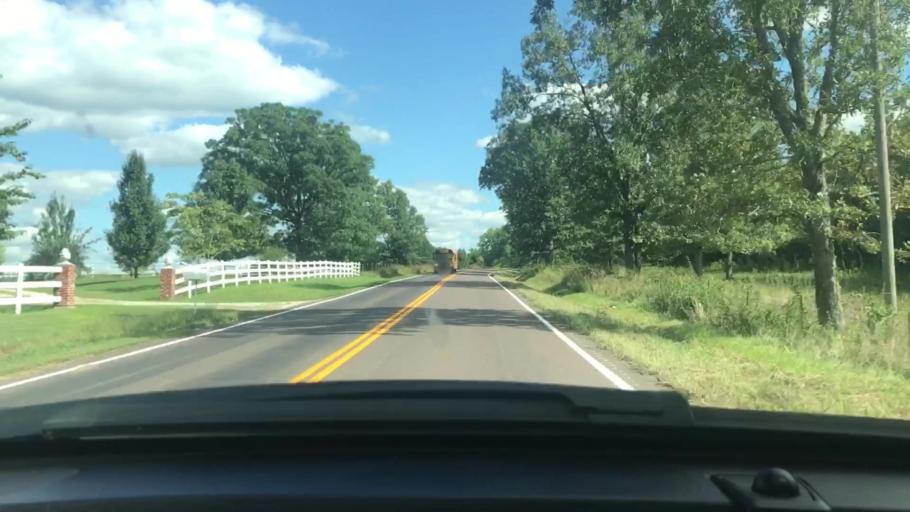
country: US
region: Missouri
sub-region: Wright County
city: Mountain Grove
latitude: 37.2315
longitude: -92.2961
